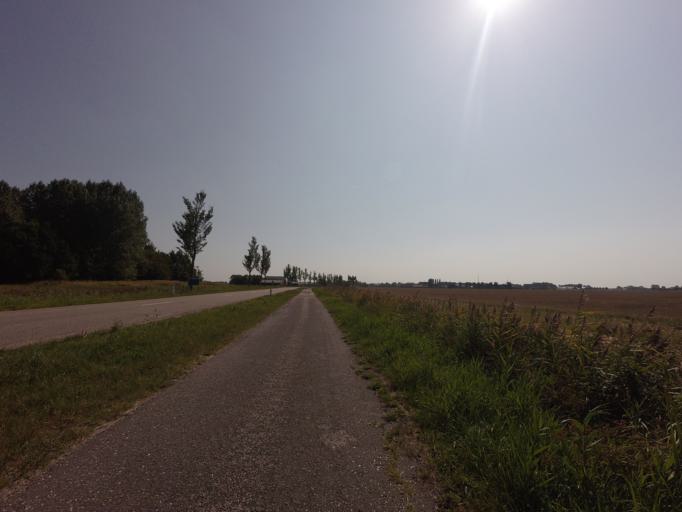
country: NL
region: Groningen
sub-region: Gemeente Zuidhorn
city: Grijpskerk
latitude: 53.2747
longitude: 6.3043
